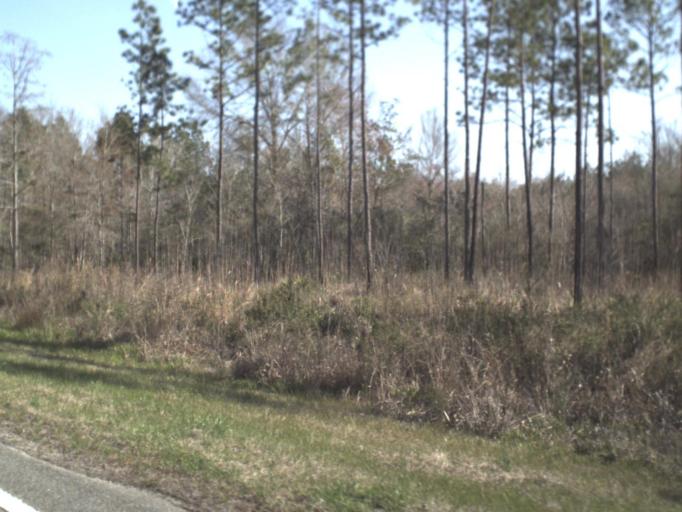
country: US
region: Florida
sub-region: Leon County
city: Woodville
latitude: 30.2526
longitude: -84.0426
